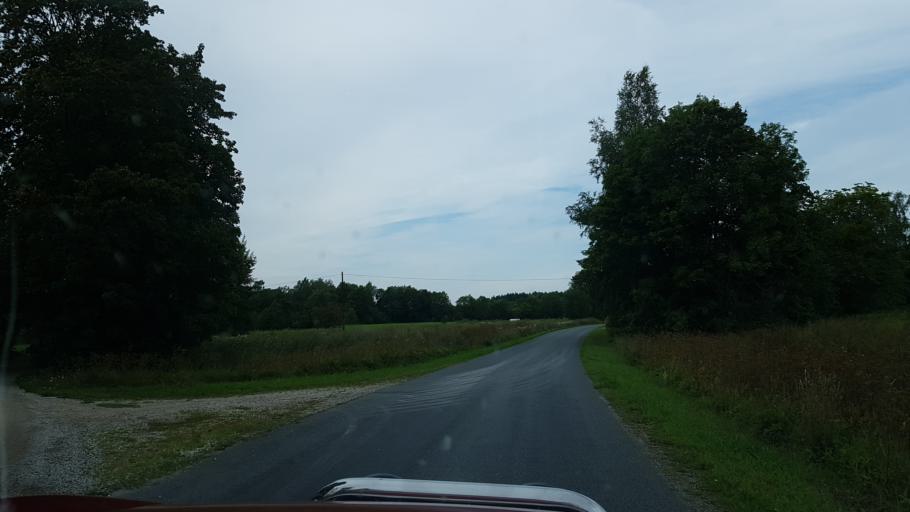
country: EE
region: Laeaene
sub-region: Ridala Parish
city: Uuemoisa
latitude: 59.0144
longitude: 23.7221
